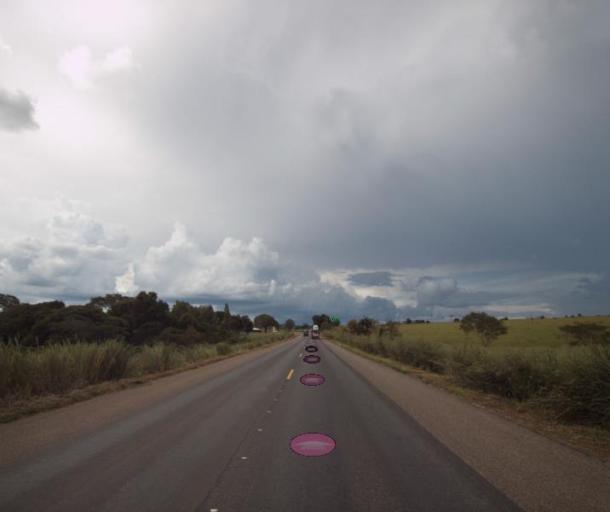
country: BR
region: Goias
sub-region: Ceres
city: Ceres
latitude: -15.2150
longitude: -49.5493
